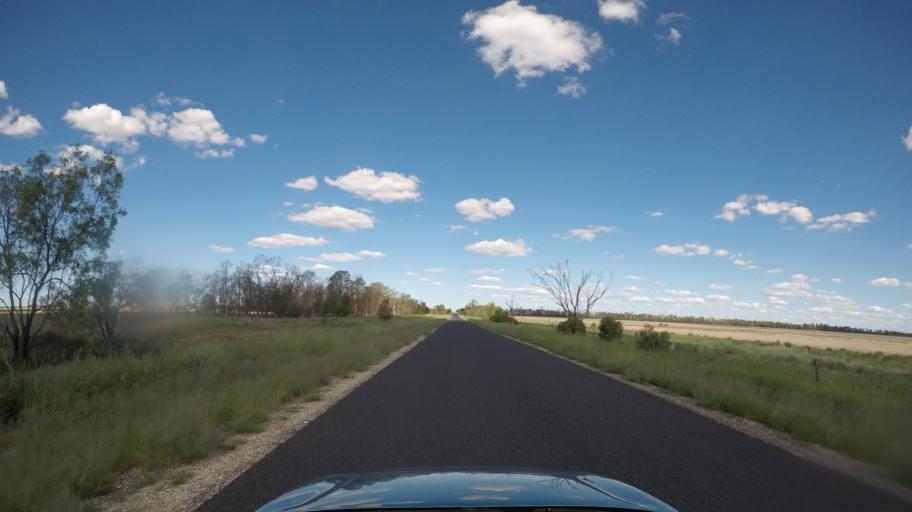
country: AU
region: Queensland
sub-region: Goondiwindi
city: Goondiwindi
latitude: -28.1650
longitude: 150.1696
